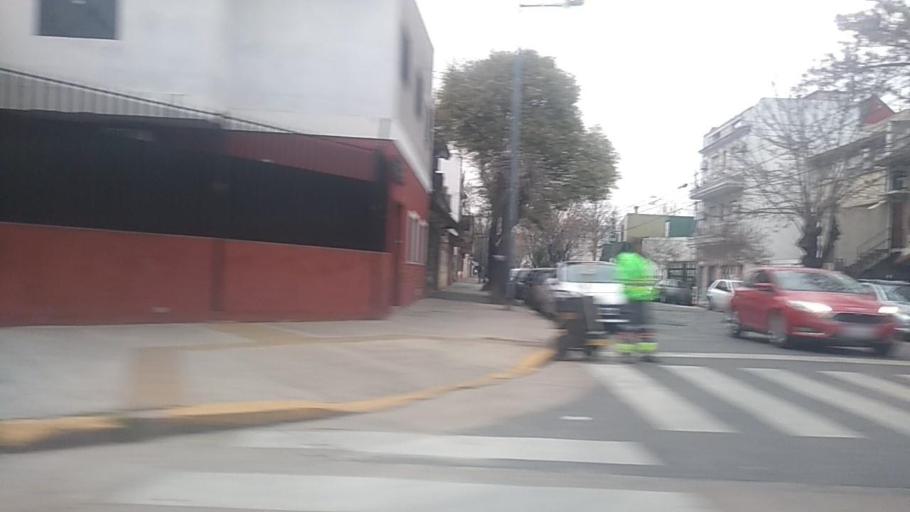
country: AR
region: Buenos Aires F.D.
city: Villa Santa Rita
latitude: -34.6030
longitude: -58.4998
